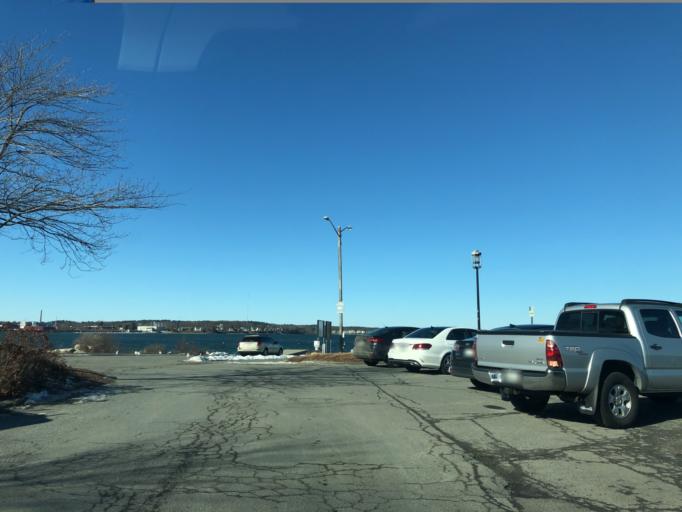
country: US
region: Maine
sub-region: Cumberland County
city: Portland
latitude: 43.6701
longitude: -70.2414
